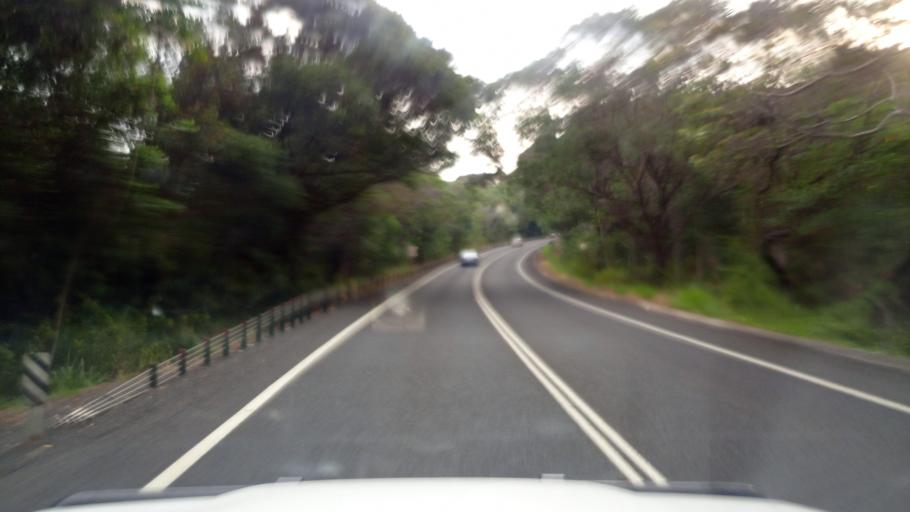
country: AU
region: Queensland
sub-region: Tablelands
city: Kuranda
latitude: -16.8365
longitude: 145.6187
